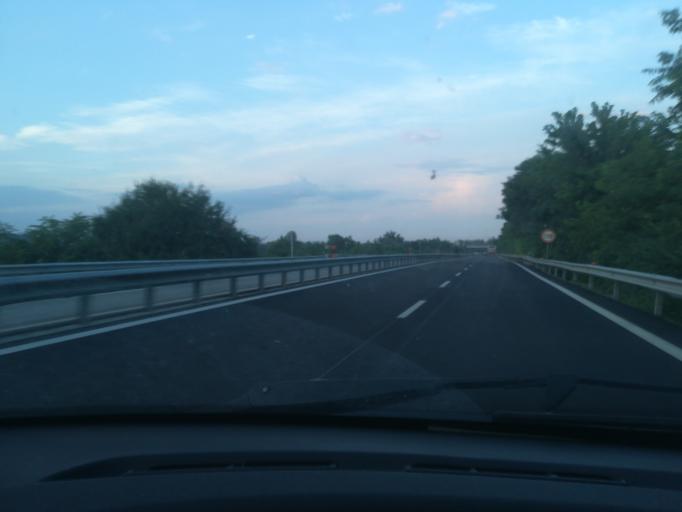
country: IT
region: The Marches
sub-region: Provincia di Macerata
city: Zona Industriale
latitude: 43.2573
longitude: 13.4595
